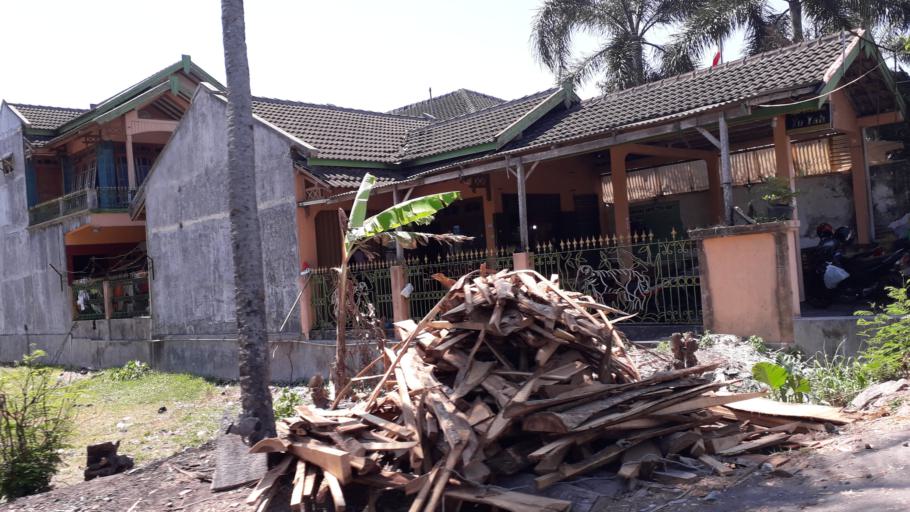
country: ID
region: Daerah Istimewa Yogyakarta
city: Pundong
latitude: -7.9800
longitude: 110.3170
